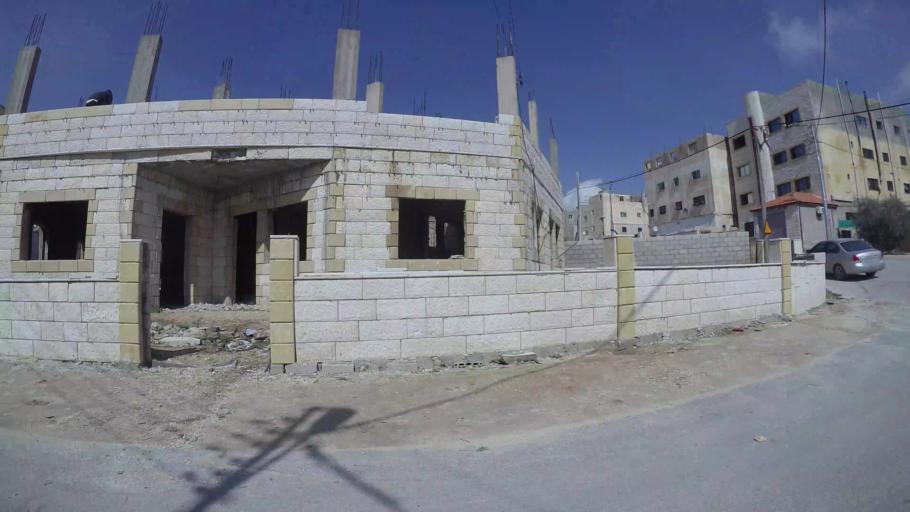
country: JO
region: Amman
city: Al Bunayyat ash Shamaliyah
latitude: 31.9020
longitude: 35.9049
